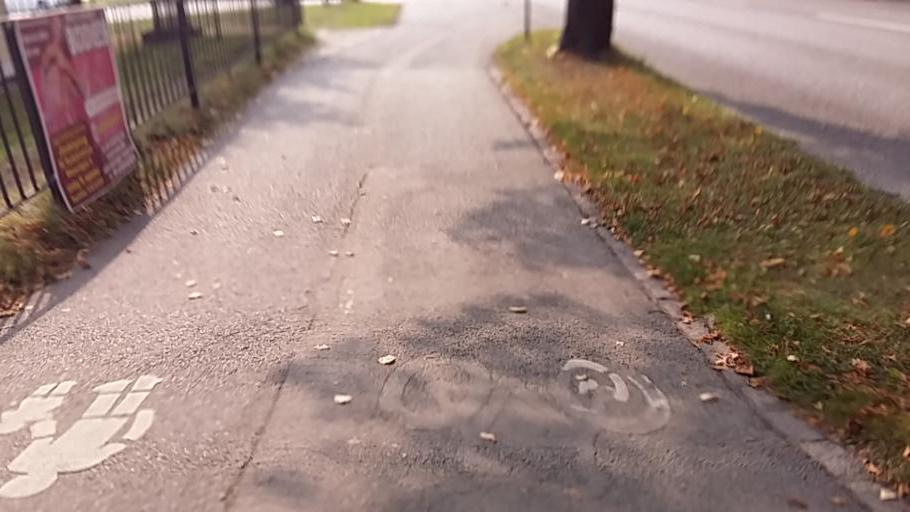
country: SE
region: Joenkoeping
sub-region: Jonkopings Kommun
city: Jonkoping
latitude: 57.7735
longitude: 14.1572
